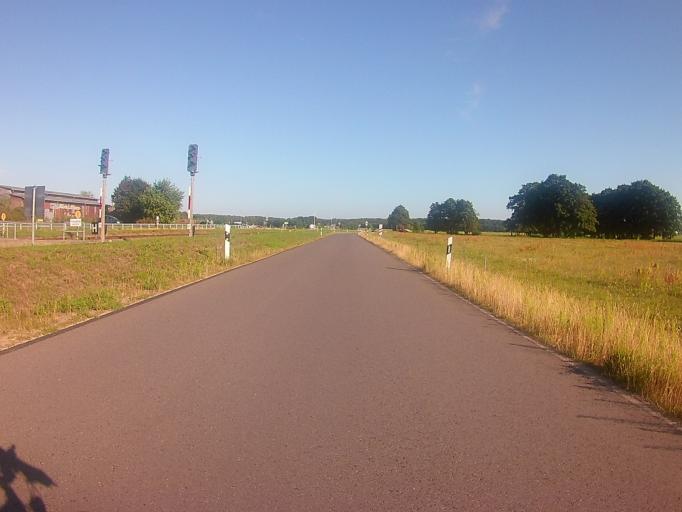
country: DE
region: Mecklenburg-Vorpommern
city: Koserow
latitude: 54.0449
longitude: 13.9996
